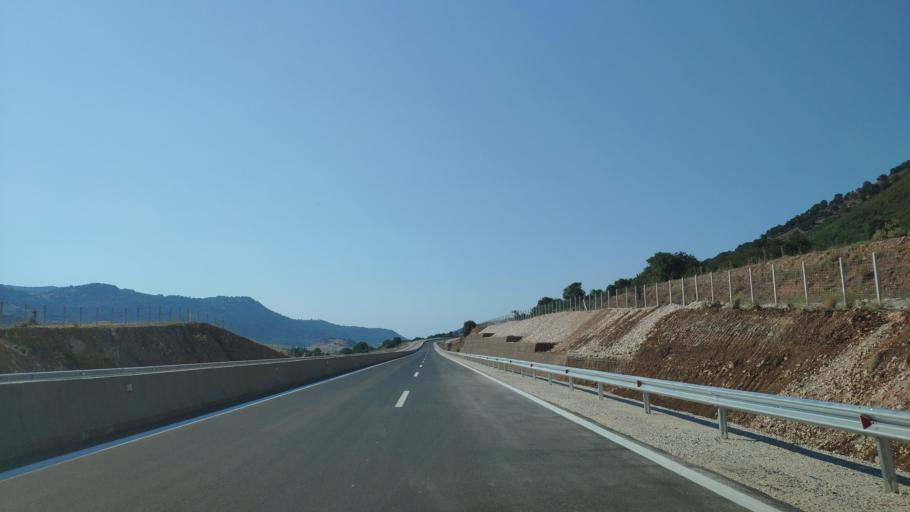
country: GR
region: West Greece
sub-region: Nomos Aitolias kai Akarnanias
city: Katouna
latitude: 38.7975
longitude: 21.1369
